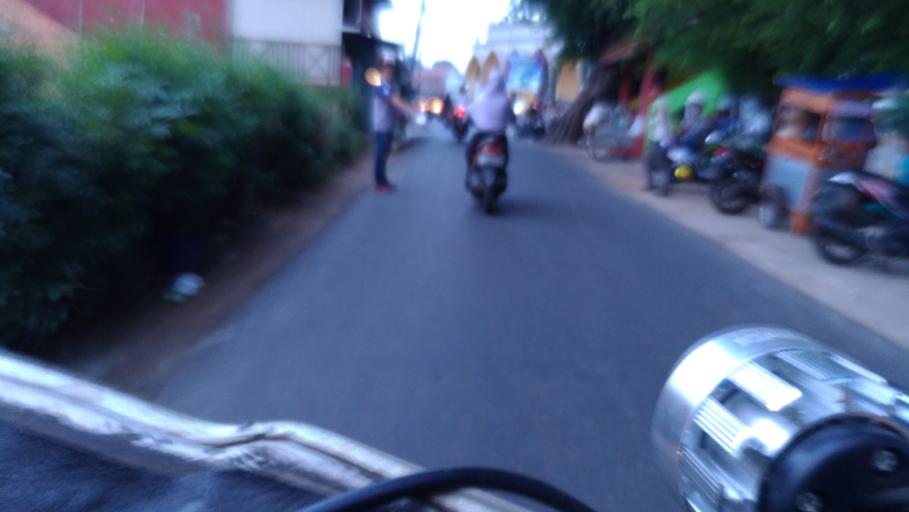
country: ID
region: West Java
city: Depok
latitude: -6.3536
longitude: 106.8688
